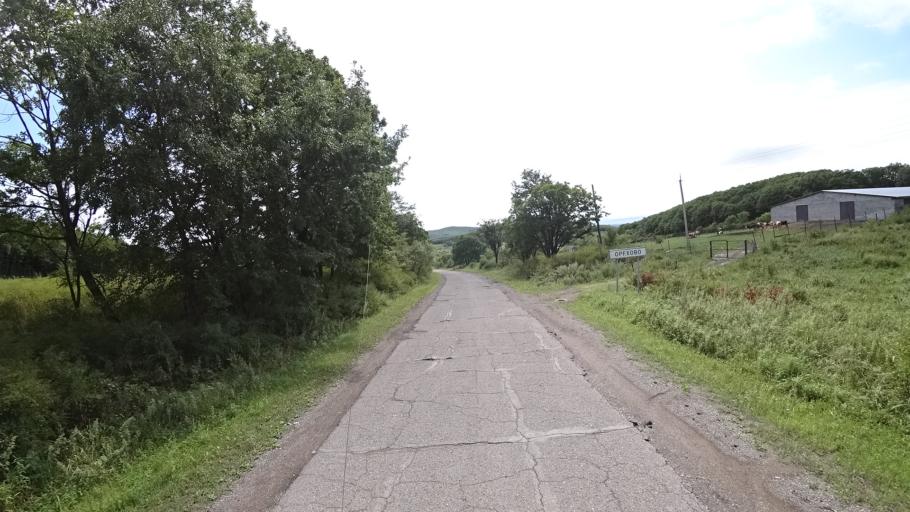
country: RU
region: Primorskiy
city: Lyalichi
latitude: 44.1423
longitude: 132.3887
